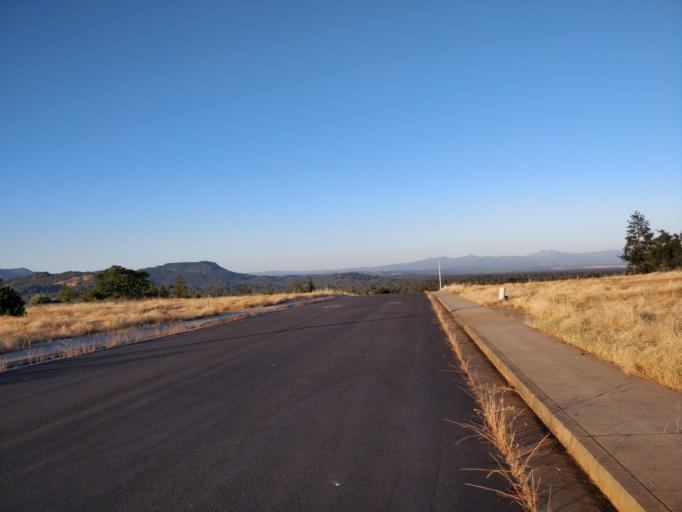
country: US
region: California
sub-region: Shasta County
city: Shasta Lake
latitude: 40.6630
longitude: -122.3671
